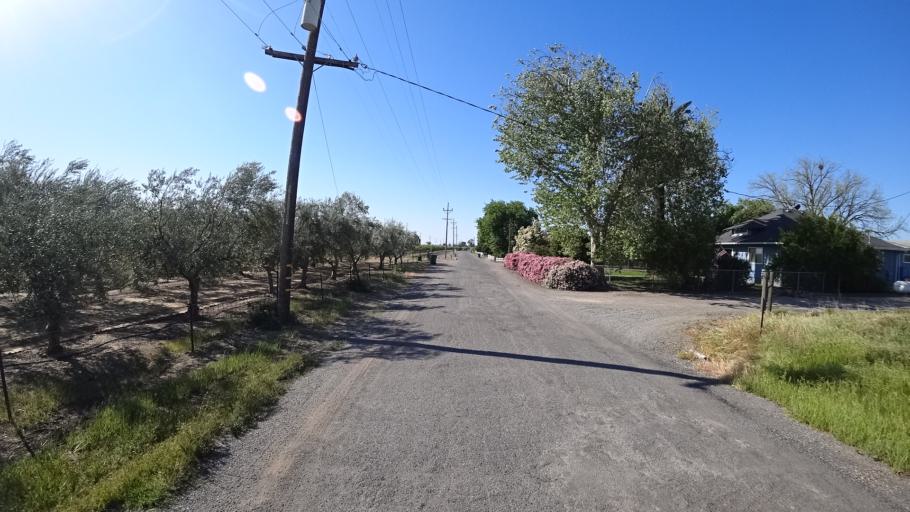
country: US
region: California
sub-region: Glenn County
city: Orland
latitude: 39.7529
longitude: -122.1692
